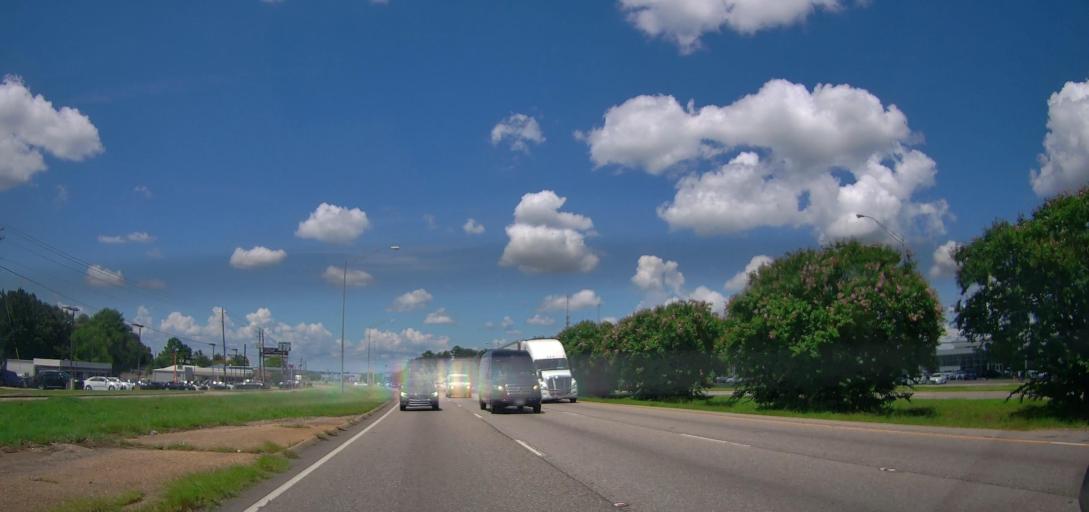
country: US
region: Alabama
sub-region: Montgomery County
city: Montgomery
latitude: 32.3691
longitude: -86.2104
